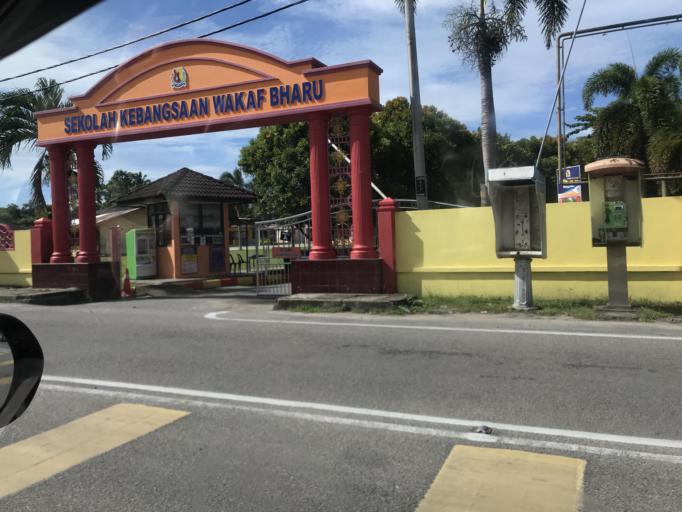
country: MY
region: Kelantan
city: Kota Bharu
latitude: 6.1187
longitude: 102.1971
